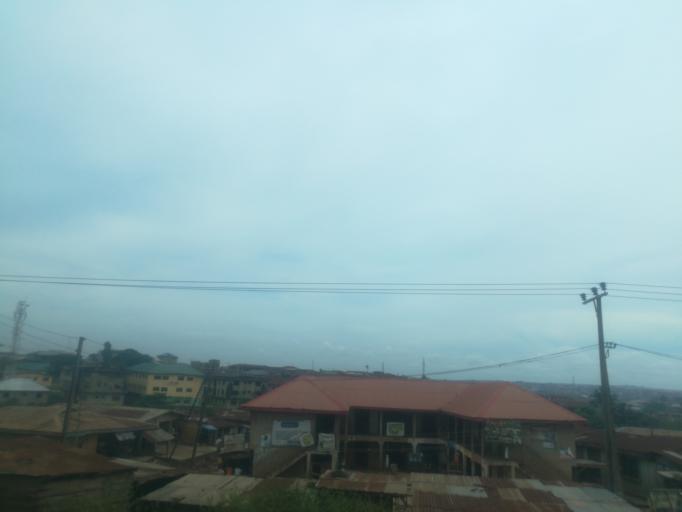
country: NG
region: Oyo
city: Ibadan
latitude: 7.3694
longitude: 3.9292
